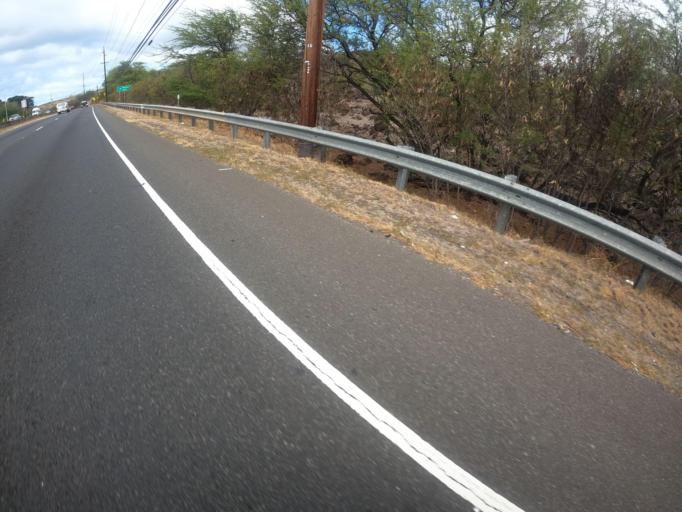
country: US
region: Hawaii
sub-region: Honolulu County
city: Makakilo City
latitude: 21.3430
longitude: -158.1106
